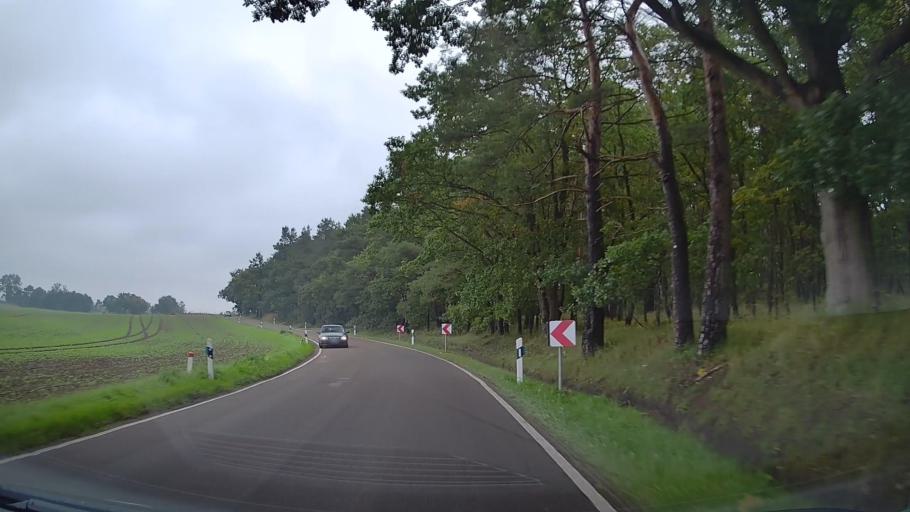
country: DE
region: Mecklenburg-Vorpommern
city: Blowatz
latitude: 53.9690
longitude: 11.5538
